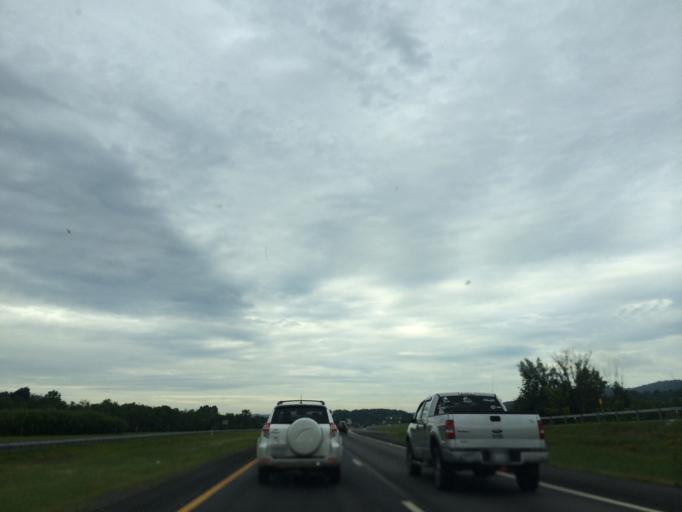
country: US
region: New York
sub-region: Greene County
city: Coxsackie
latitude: 42.3929
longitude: -73.8253
